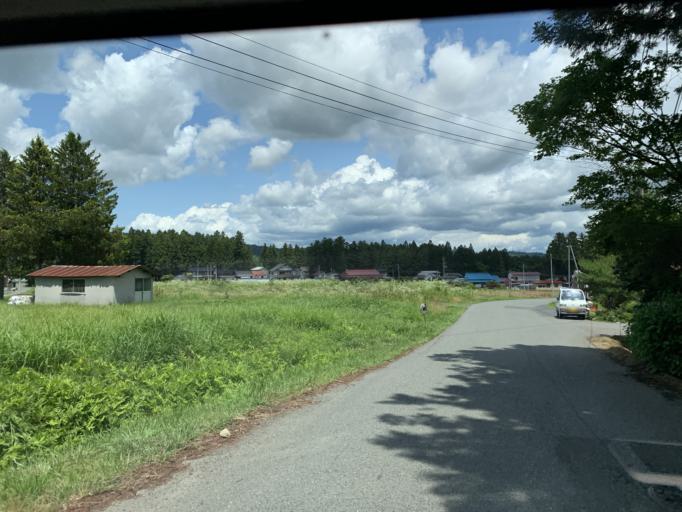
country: JP
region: Iwate
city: Ichinoseki
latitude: 38.9292
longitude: 141.0782
